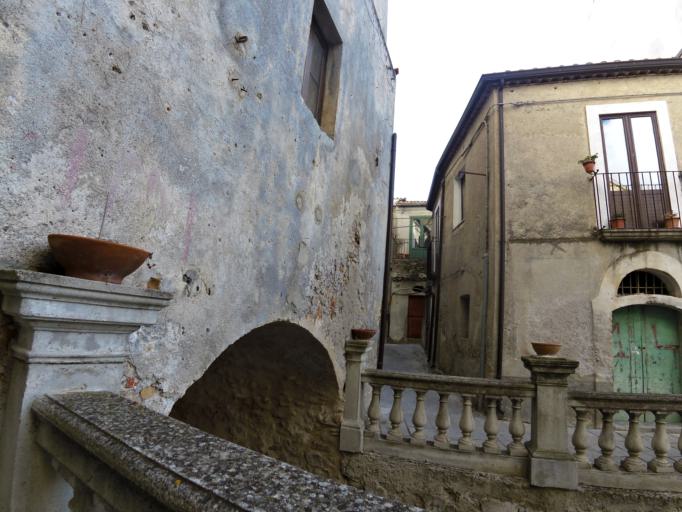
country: IT
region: Calabria
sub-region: Provincia di Reggio Calabria
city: Caulonia
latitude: 38.3823
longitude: 16.4071
